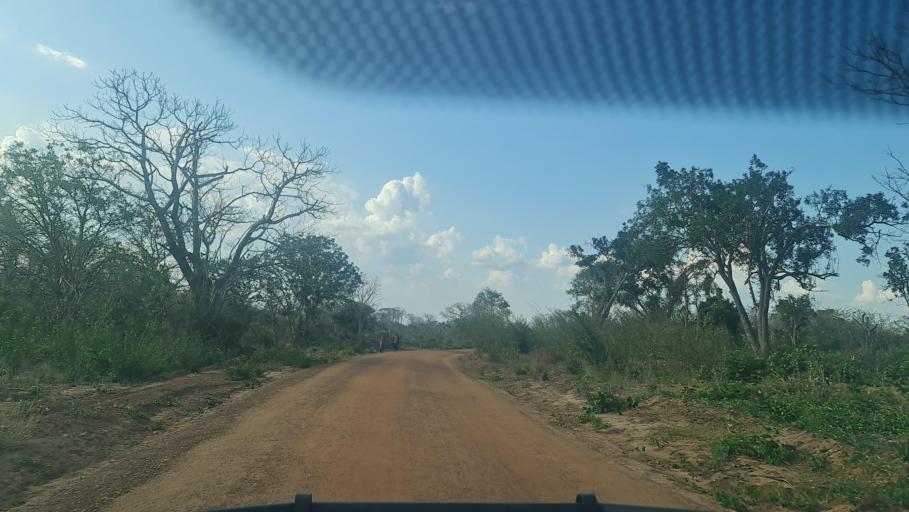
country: MZ
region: Nampula
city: Ilha de Mocambique
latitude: -15.5129
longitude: 40.1639
